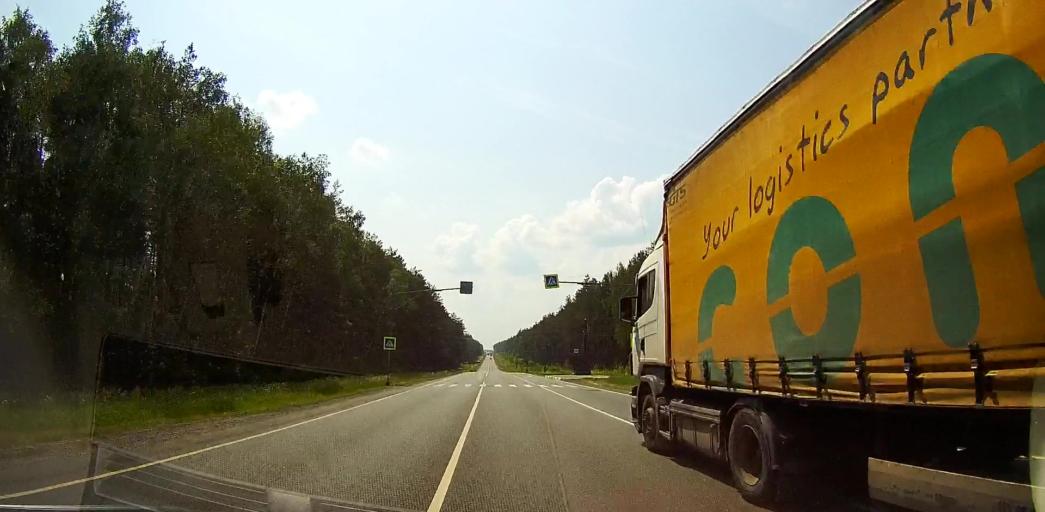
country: RU
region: Moskovskaya
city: Meshcherino
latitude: 55.1724
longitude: 38.3308
